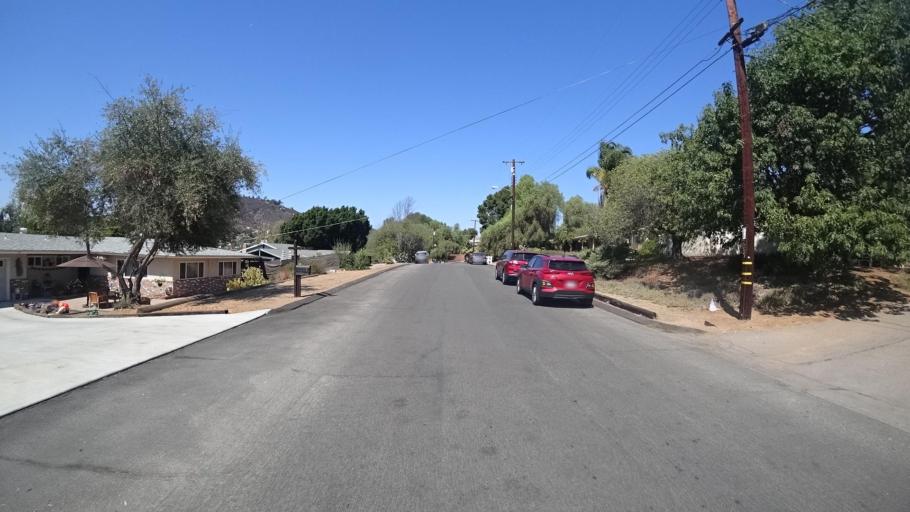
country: US
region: California
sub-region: San Diego County
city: Winter Gardens
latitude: 32.8251
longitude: -116.9278
